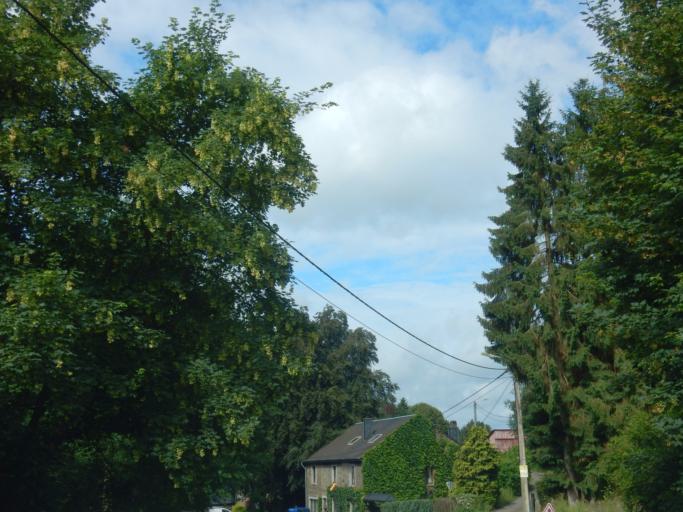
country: BE
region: Wallonia
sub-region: Province de Namur
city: Bievre
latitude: 49.8992
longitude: 5.0255
